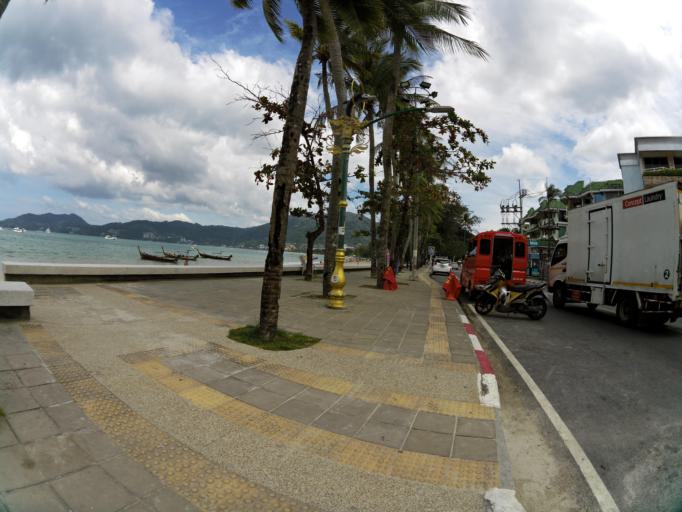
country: TH
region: Phuket
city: Patong
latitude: 7.8865
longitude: 98.2906
